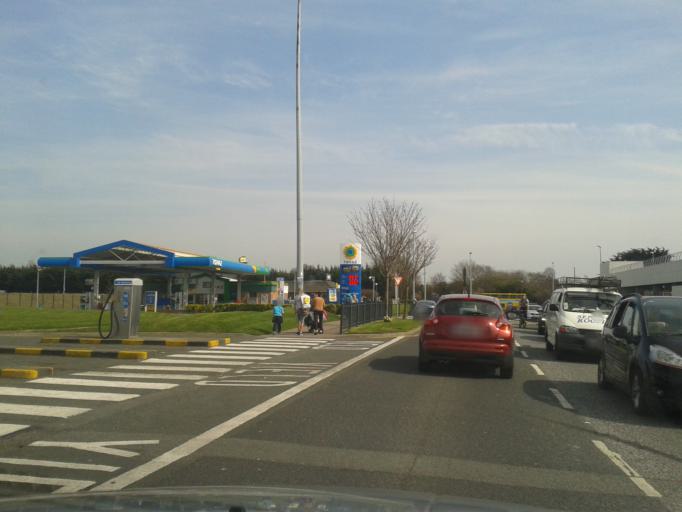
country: IE
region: Leinster
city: Beaumont
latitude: 53.3932
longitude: -6.2481
